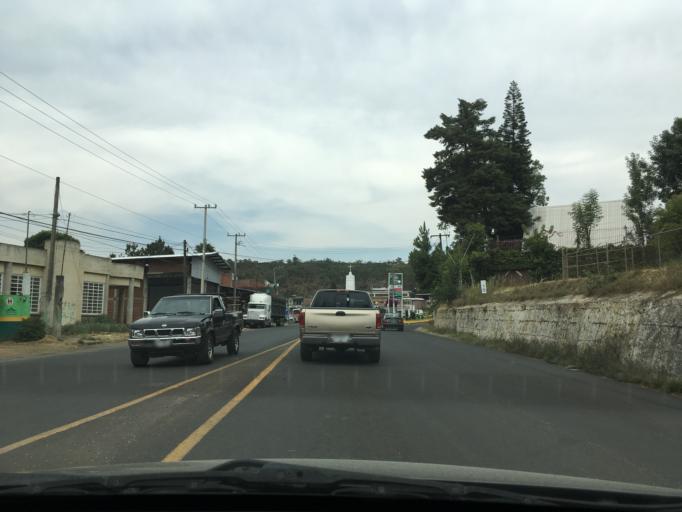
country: MX
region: Michoacan
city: Nuevo San Juan Parangaricutiro
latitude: 19.4113
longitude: -102.1158
